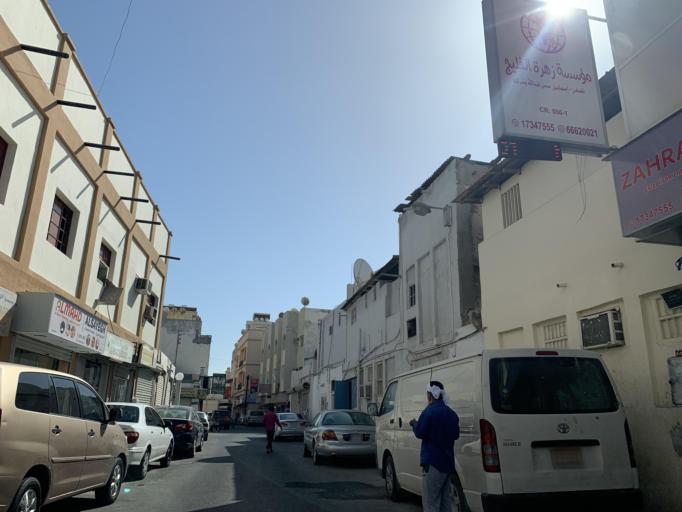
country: BH
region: Muharraq
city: Al Muharraq
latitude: 26.2490
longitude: 50.6137
